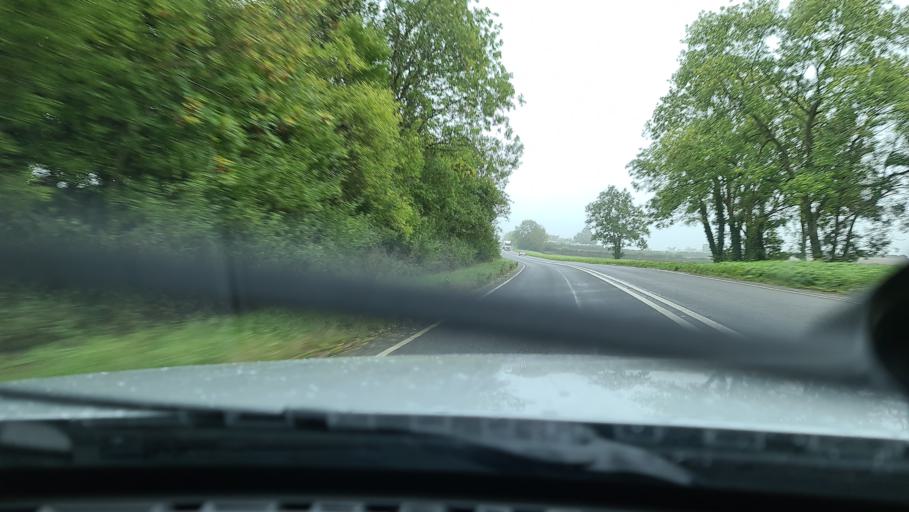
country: GB
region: England
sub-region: Oxfordshire
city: Deddington
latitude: 51.9651
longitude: -1.3207
